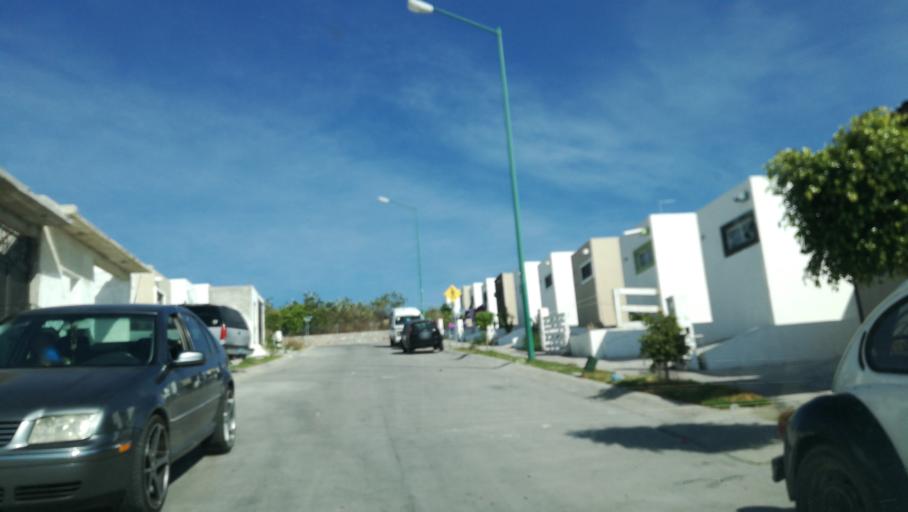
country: MX
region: Guanajuato
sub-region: Leon
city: La Ermita
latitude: 21.1603
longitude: -101.7388
